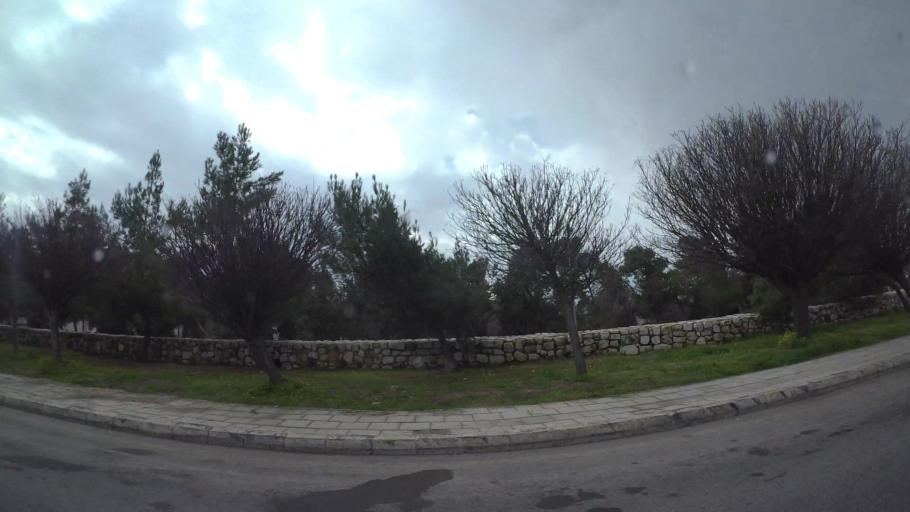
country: JO
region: Amman
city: Wadi as Sir
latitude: 31.9803
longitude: 35.8273
